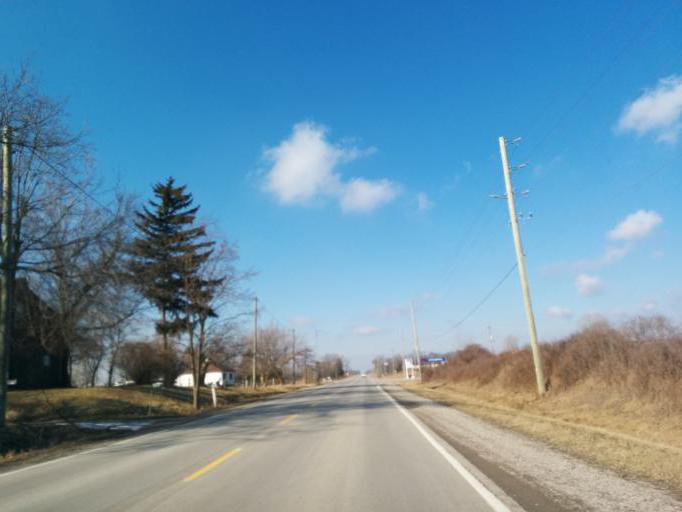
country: CA
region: Ontario
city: Brantford
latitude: 43.0036
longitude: -80.1645
